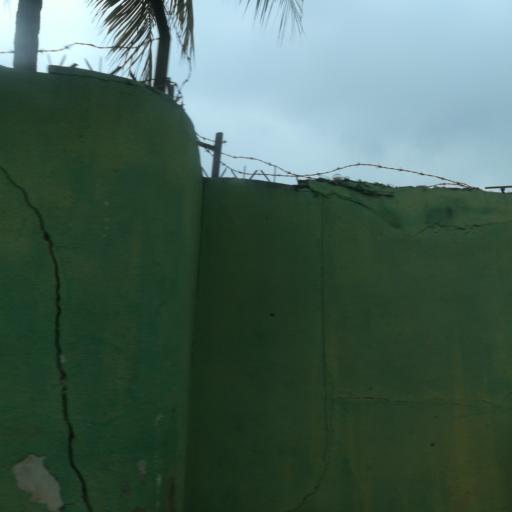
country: NG
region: Lagos
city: Agege
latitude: 6.5921
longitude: 3.2977
